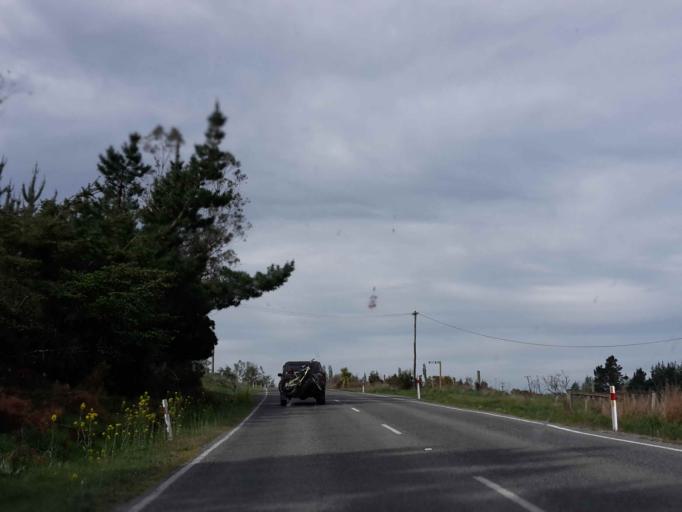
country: NZ
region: Canterbury
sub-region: Timaru District
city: Pleasant Point
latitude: -44.1245
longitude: 171.1029
